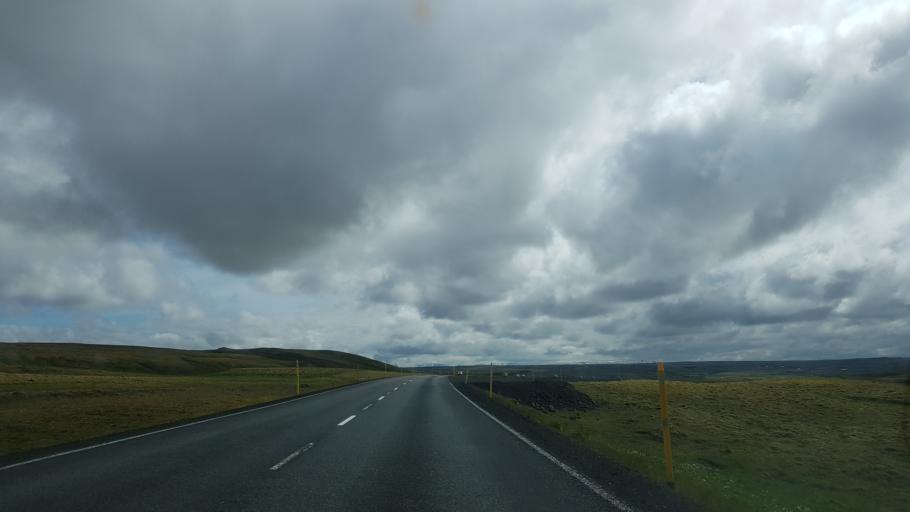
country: IS
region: West
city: Borgarnes
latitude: 64.9656
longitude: -21.0633
